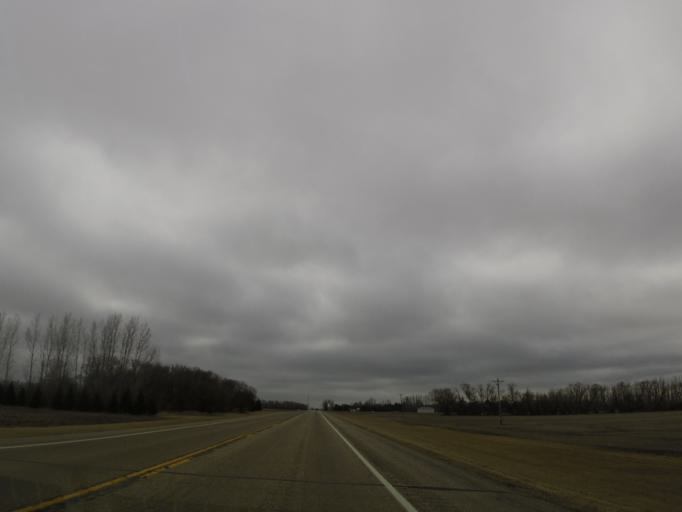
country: US
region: North Dakota
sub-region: Cass County
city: Casselton
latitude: 46.6615
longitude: -97.2414
